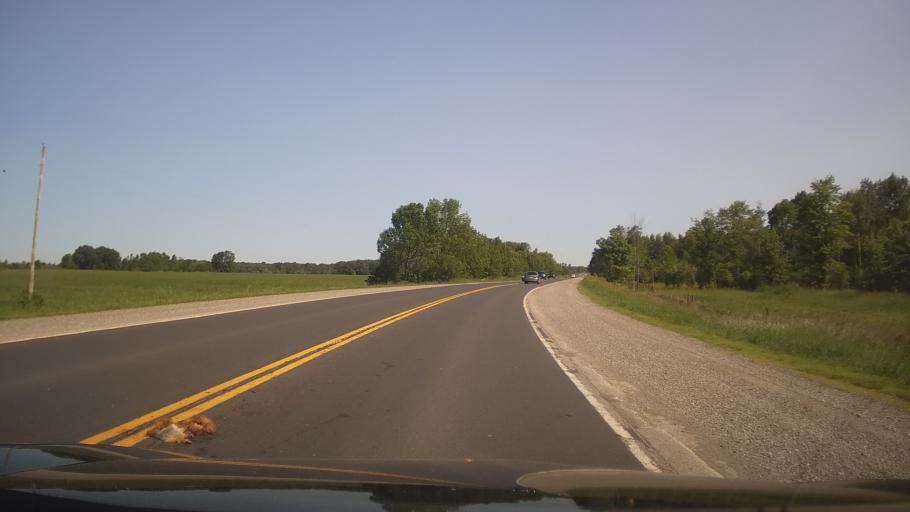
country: CA
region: Ontario
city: Omemee
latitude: 44.3145
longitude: -78.6801
